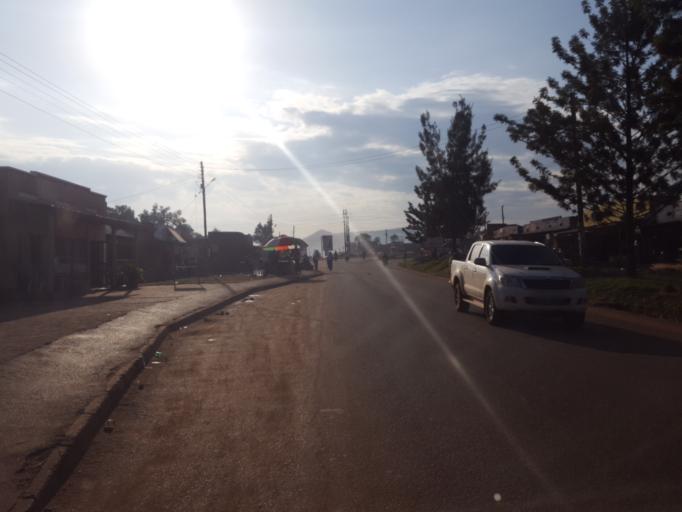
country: UG
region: Western Region
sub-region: Hoima District
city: Hoima
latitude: 1.4217
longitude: 31.3698
